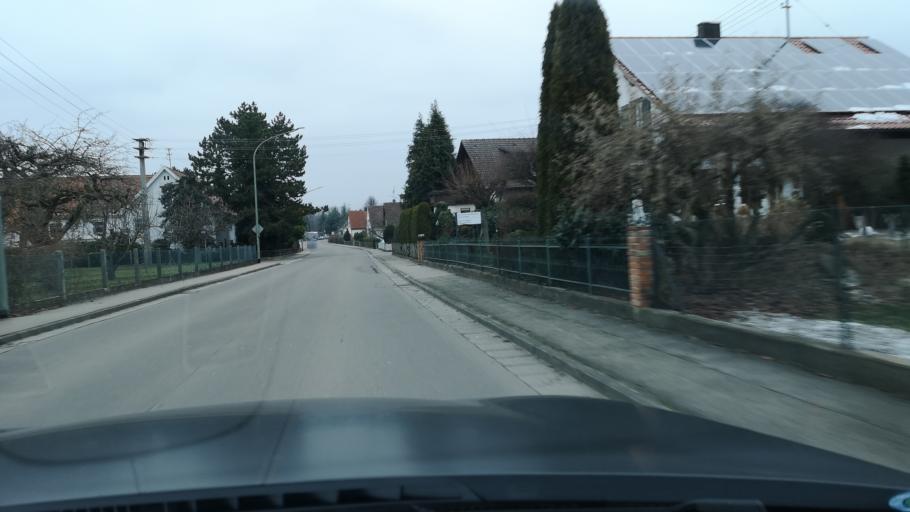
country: DE
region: Bavaria
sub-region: Swabia
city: Leipheim
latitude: 48.4279
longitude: 10.1903
